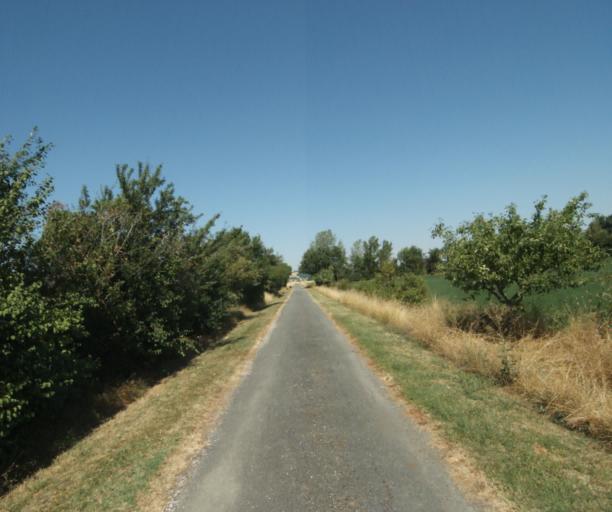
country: FR
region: Midi-Pyrenees
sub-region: Departement de la Haute-Garonne
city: Revel
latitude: 43.5113
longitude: 1.9584
